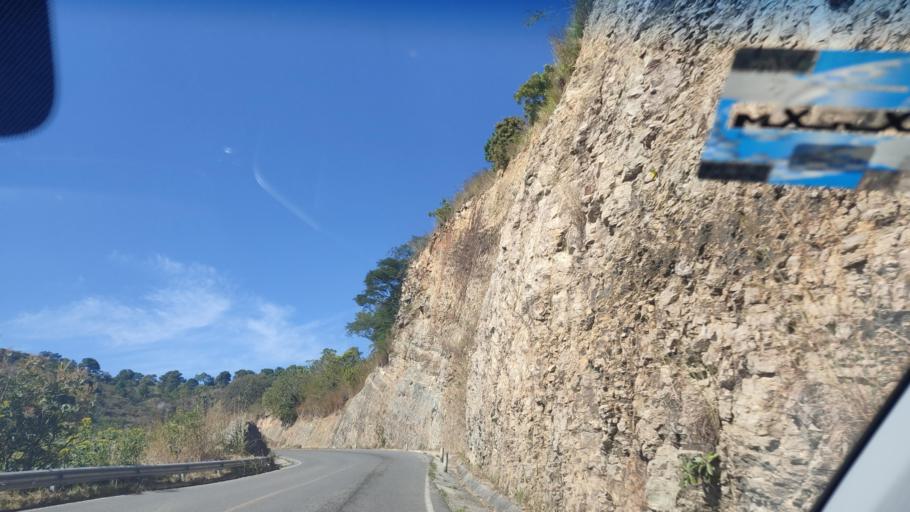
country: MX
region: Nayarit
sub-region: Jala
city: Rosa Blanca
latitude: 21.0929
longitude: -104.3816
